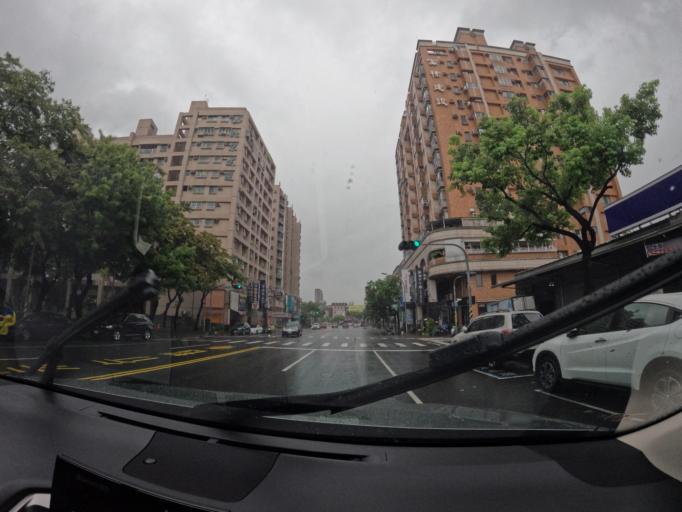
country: TW
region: Kaohsiung
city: Kaohsiung
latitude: 22.6600
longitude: 120.3239
